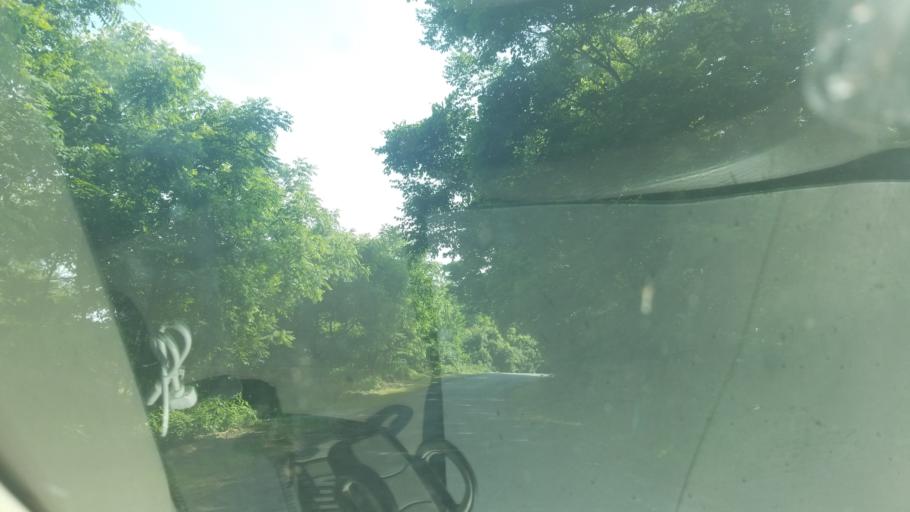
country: US
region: Ohio
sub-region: Champaign County
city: North Lewisburg
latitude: 40.2777
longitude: -83.6426
